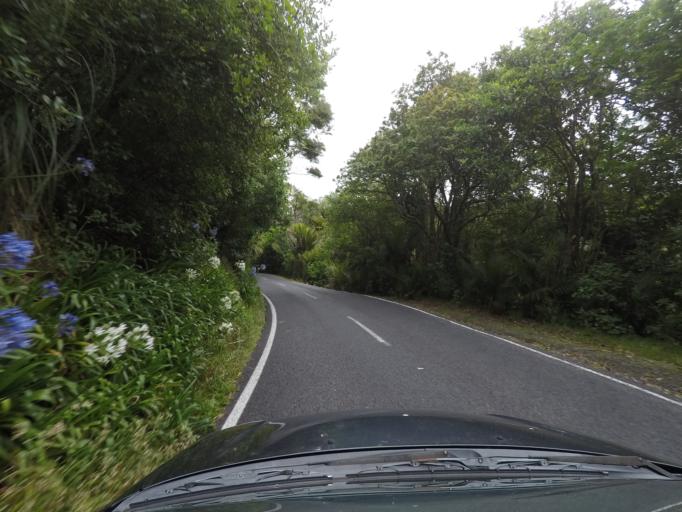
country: NZ
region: Auckland
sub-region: Auckland
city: Titirangi
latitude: -36.9451
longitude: 174.6593
